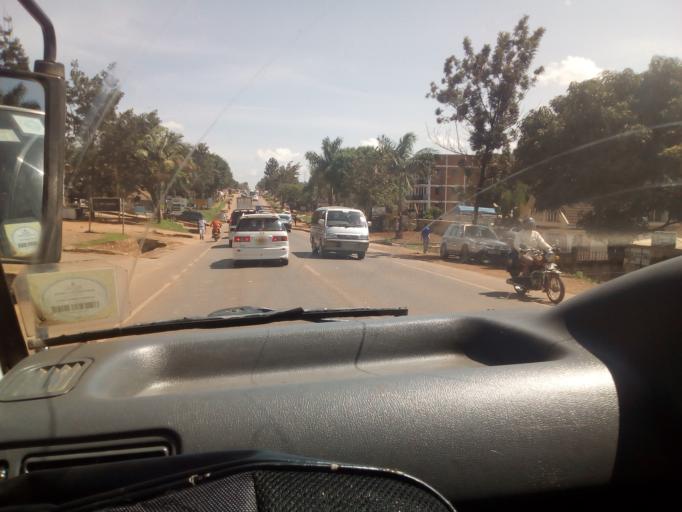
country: UG
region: Central Region
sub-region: Wakiso District
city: Kajansi
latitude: 0.2403
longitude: 32.5558
